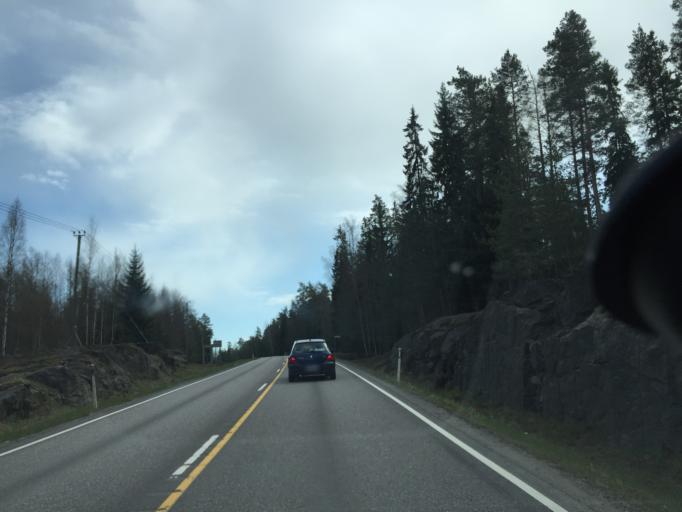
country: FI
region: Uusimaa
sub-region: Raaseporin
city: Ekenaes
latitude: 60.0302
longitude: 23.3687
